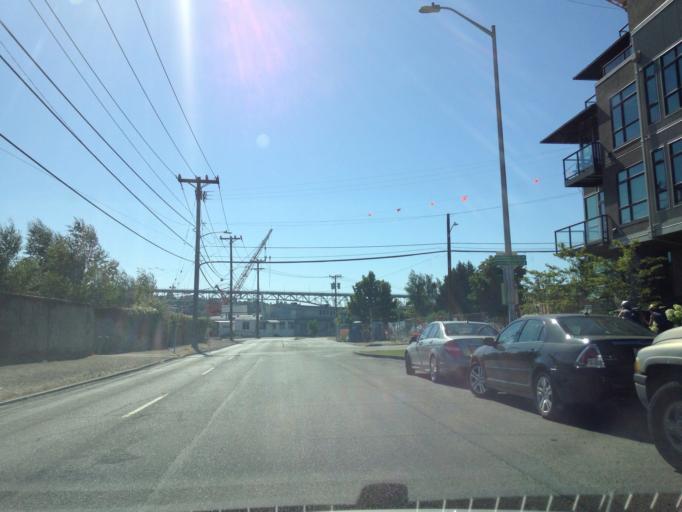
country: US
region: Washington
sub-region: King County
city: Seattle
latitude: 47.6469
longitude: -122.3369
